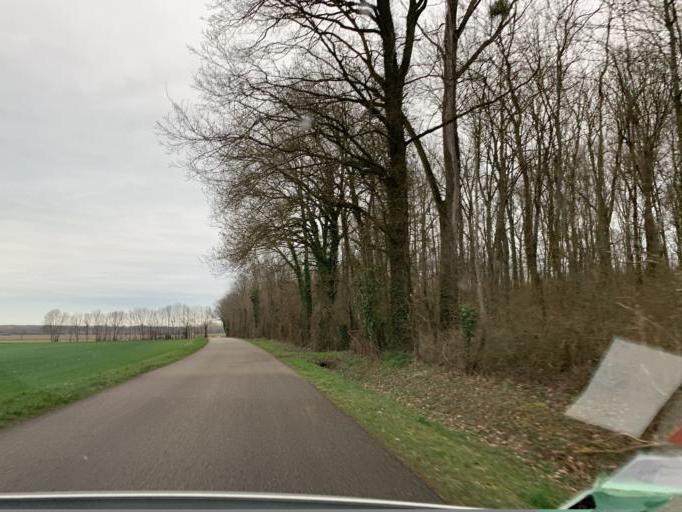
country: FR
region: Rhone-Alpes
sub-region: Departement de l'Ain
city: Mionnay
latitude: 45.8771
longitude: 4.9432
